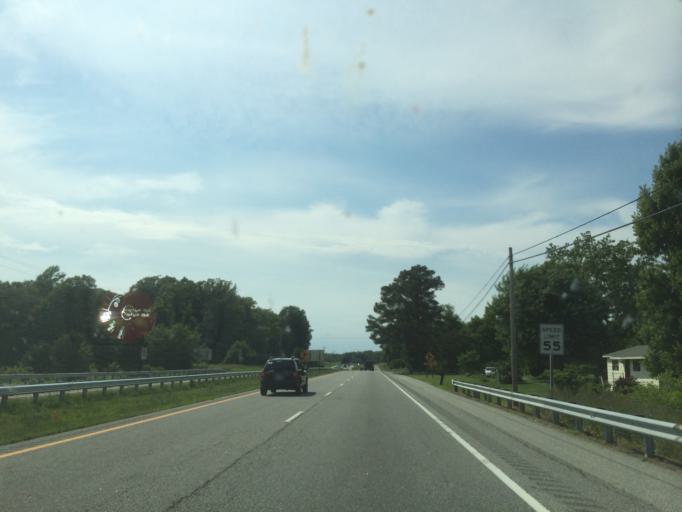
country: US
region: Maryland
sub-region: Queen Anne's County
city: Centreville
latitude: 38.9597
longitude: -76.0943
